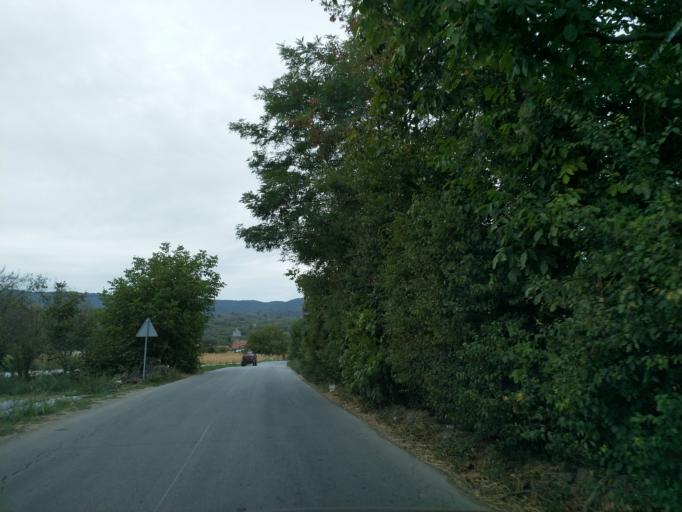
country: RS
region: Central Serbia
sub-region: Pomoravski Okrug
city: Paracin
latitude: 43.8323
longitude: 21.3317
